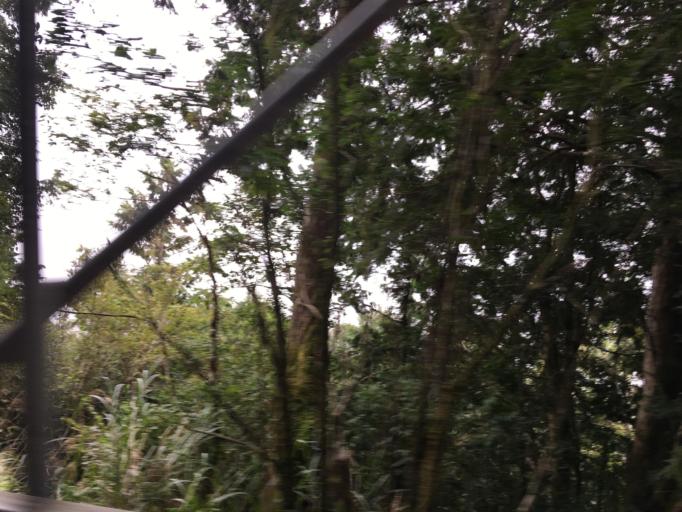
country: TW
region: Taiwan
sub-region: Yilan
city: Yilan
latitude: 24.4889
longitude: 121.5342
